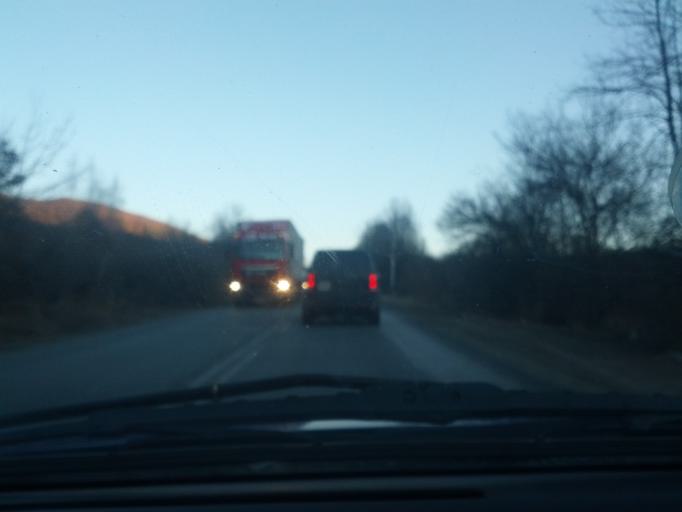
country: BG
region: Vratsa
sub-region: Obshtina Mezdra
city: Mezdra
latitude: 43.0241
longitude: 23.6696
